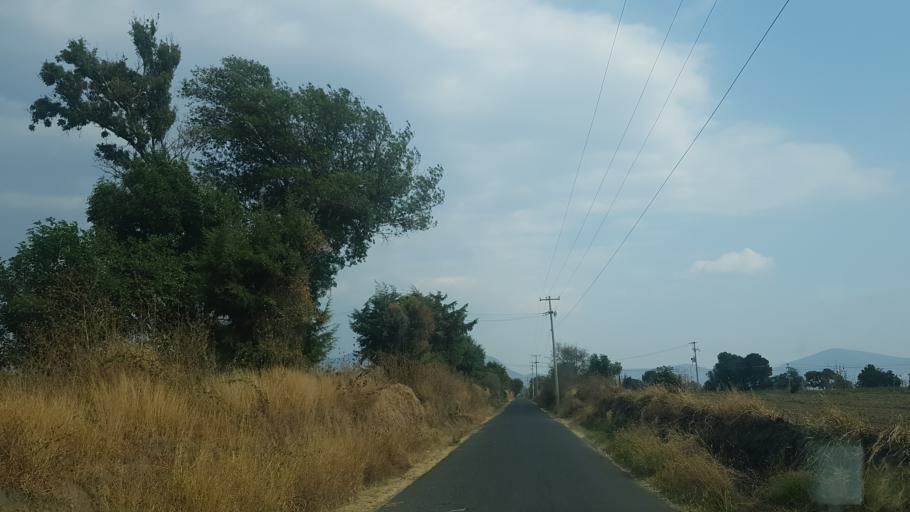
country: MX
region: Puebla
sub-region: Santa Isabel Cholula
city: Santa Ana Acozautla
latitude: 18.9555
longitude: -98.4010
